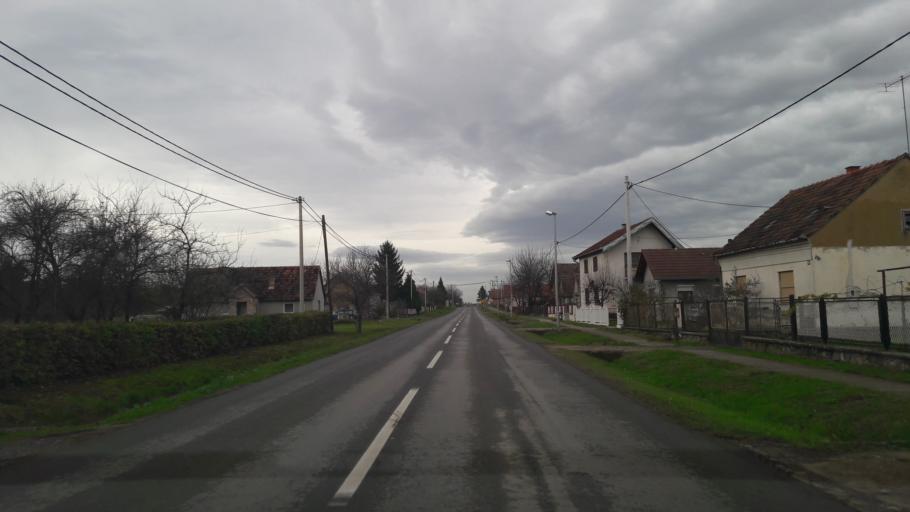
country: HR
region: Osjecko-Baranjska
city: Velimirovac
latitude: 45.5368
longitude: 18.0711
